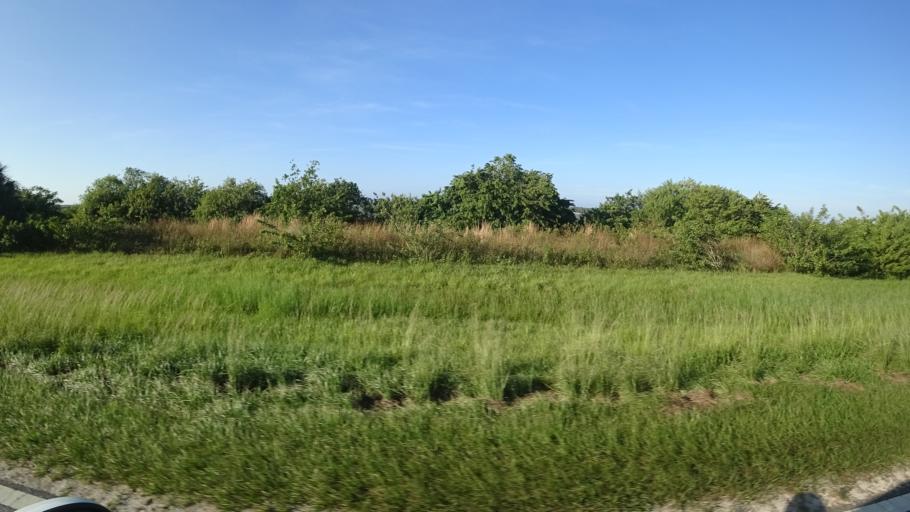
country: US
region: Florida
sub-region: Hillsborough County
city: Sun City Center
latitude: 27.5454
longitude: -82.3542
